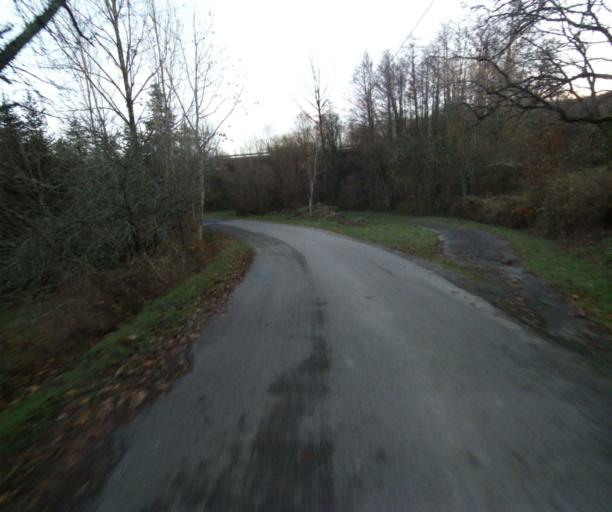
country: FR
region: Limousin
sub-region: Departement de la Correze
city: Laguenne
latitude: 45.2349
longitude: 1.7688
